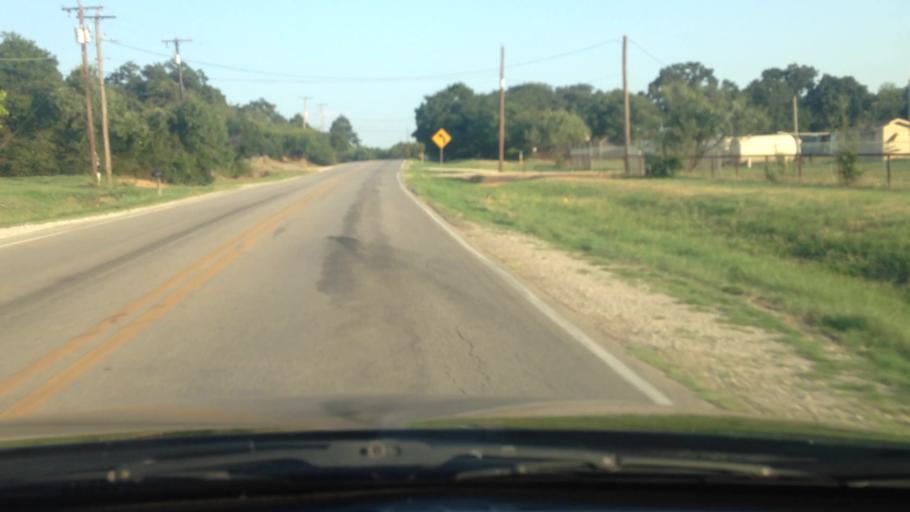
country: US
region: Texas
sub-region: Tarrant County
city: Rendon
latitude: 32.5903
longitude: -97.2513
